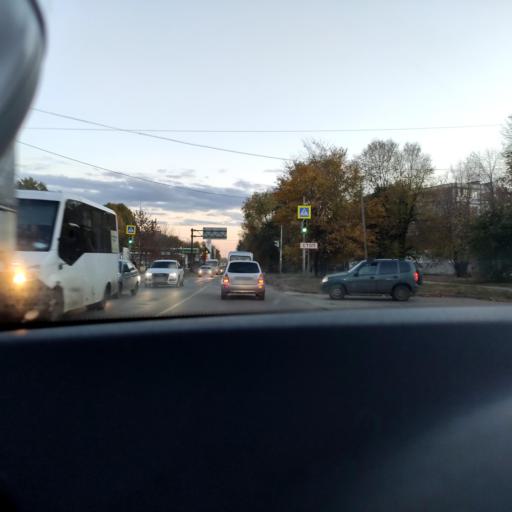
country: RU
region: Samara
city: Petra-Dubrava
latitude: 53.2486
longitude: 50.2685
